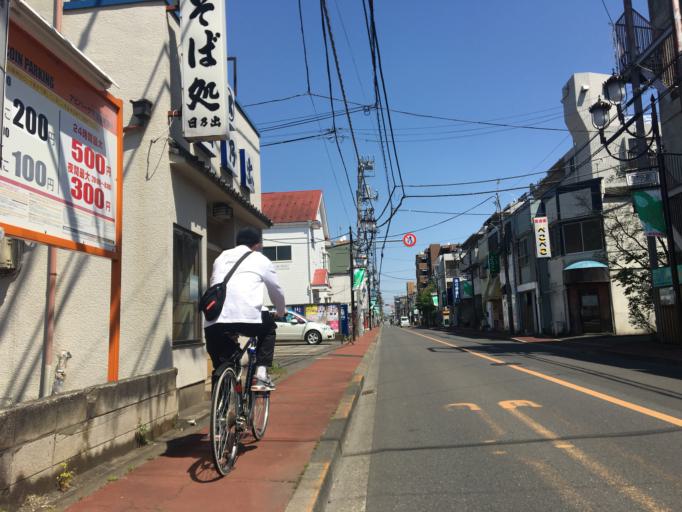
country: JP
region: Tokyo
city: Kokubunji
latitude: 35.7232
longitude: 139.4844
